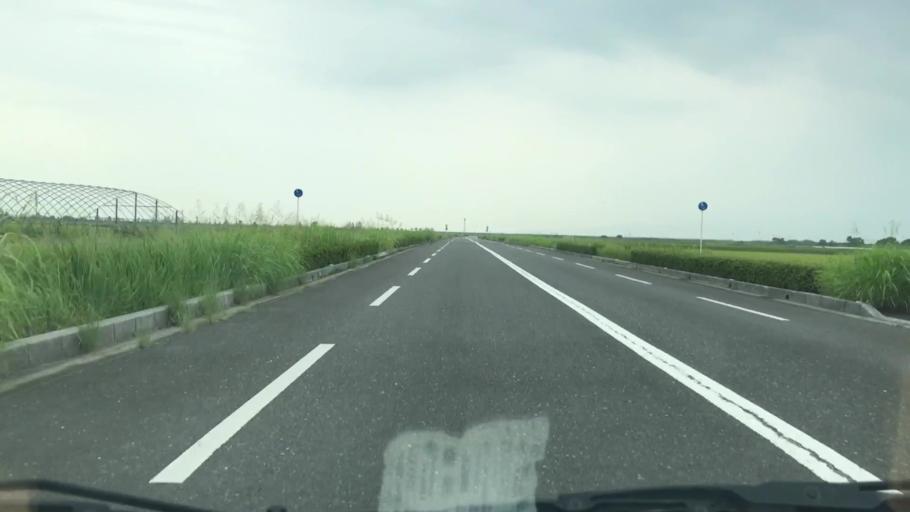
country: JP
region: Saga Prefecture
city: Okawa
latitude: 33.1708
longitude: 130.2946
